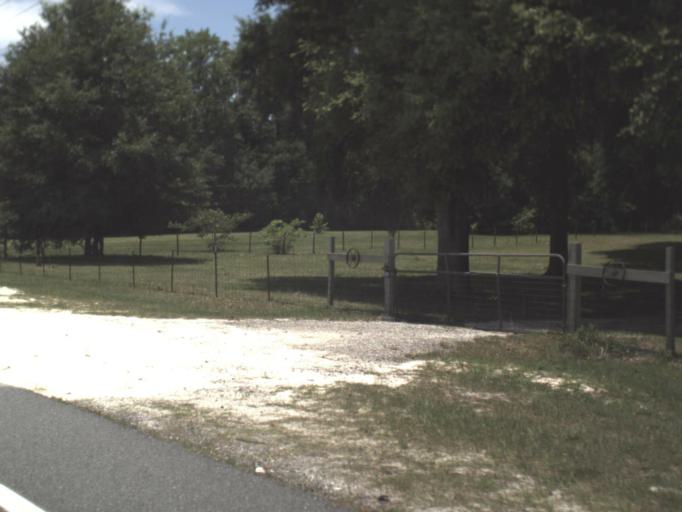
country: US
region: Florida
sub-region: Dixie County
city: Cross City
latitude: 29.7569
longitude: -82.9830
